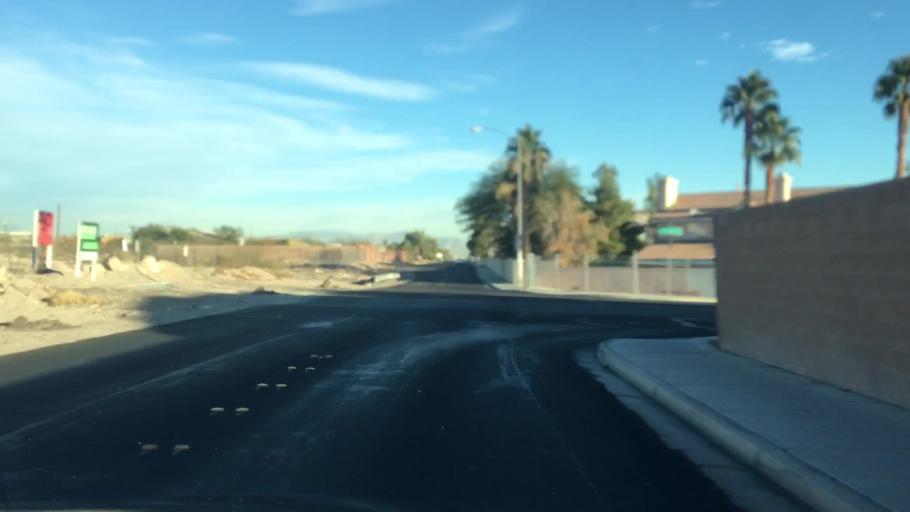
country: US
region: Nevada
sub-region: Clark County
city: Paradise
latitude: 36.0495
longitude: -115.1498
